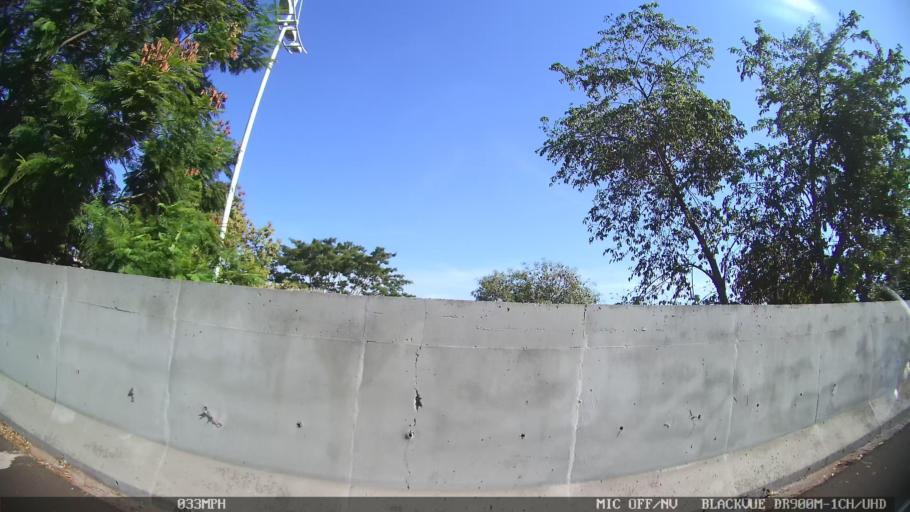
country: BR
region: Sao Paulo
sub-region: Ribeirao Preto
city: Ribeirao Preto
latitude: -21.1880
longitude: -47.7838
